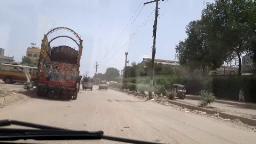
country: PK
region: Sindh
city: Malir Cantonment
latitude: 24.8402
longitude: 67.2042
